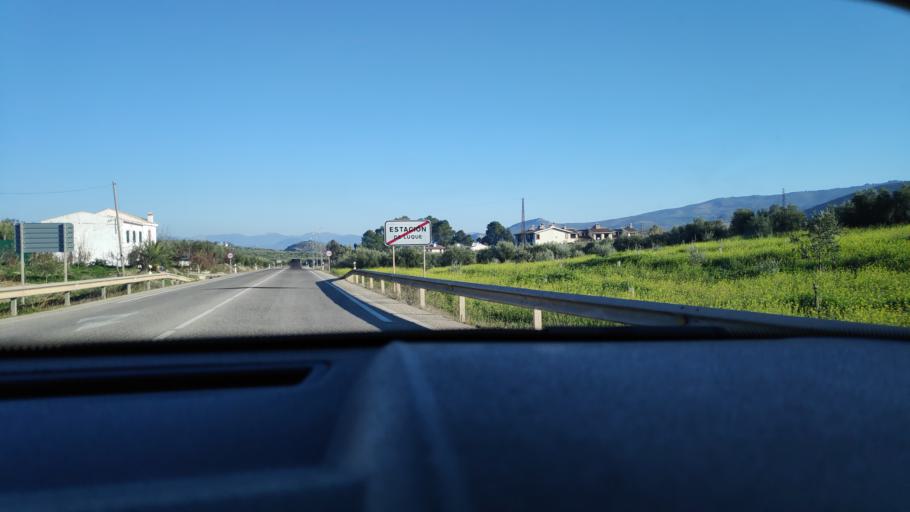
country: ES
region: Andalusia
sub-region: Province of Cordoba
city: Luque
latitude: 37.5728
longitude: -4.2583
